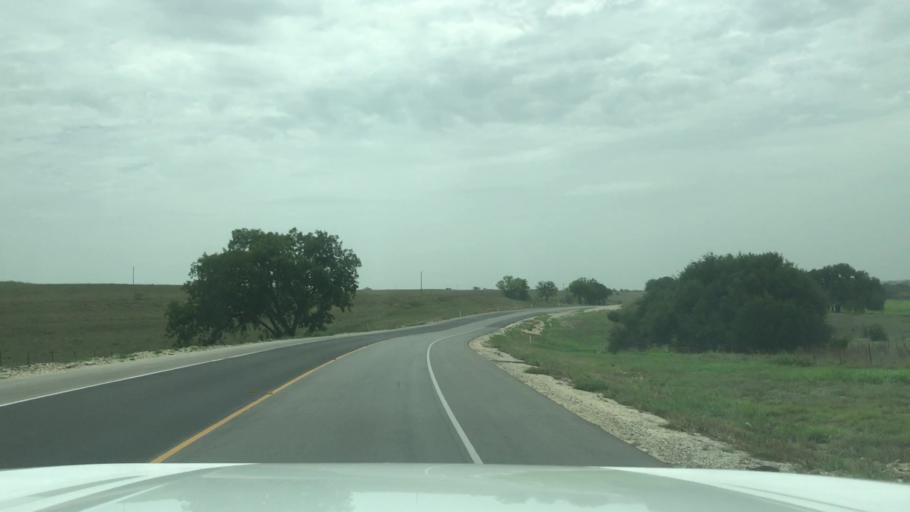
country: US
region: Texas
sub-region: Erath County
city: Dublin
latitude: 32.0723
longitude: -98.2232
